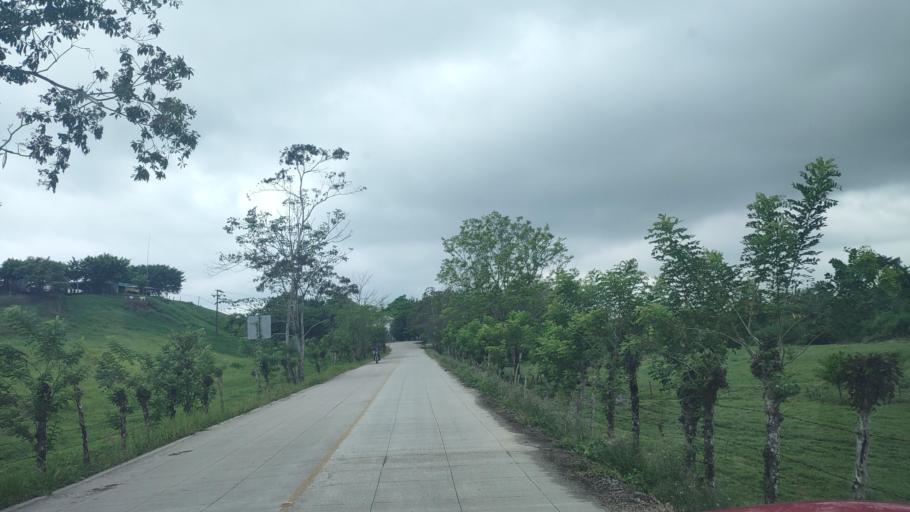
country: MX
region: Veracruz
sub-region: Uxpanapa
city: Poblado 10
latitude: 17.4943
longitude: -94.1678
